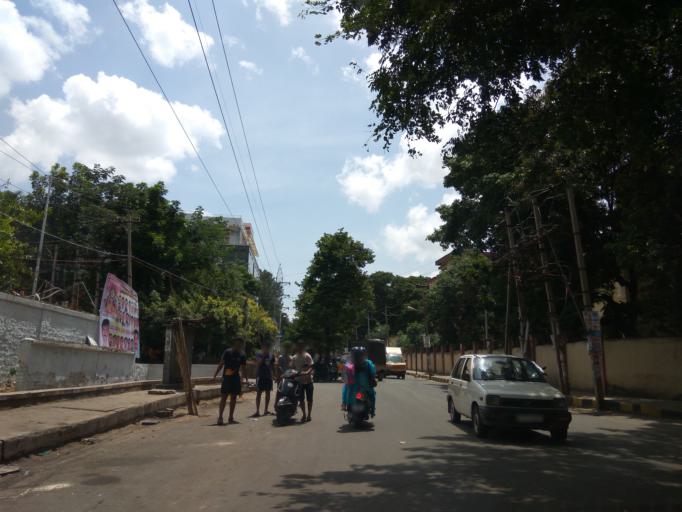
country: IN
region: Karnataka
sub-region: Bangalore Urban
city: Bangalore
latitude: 12.9852
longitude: 77.6659
